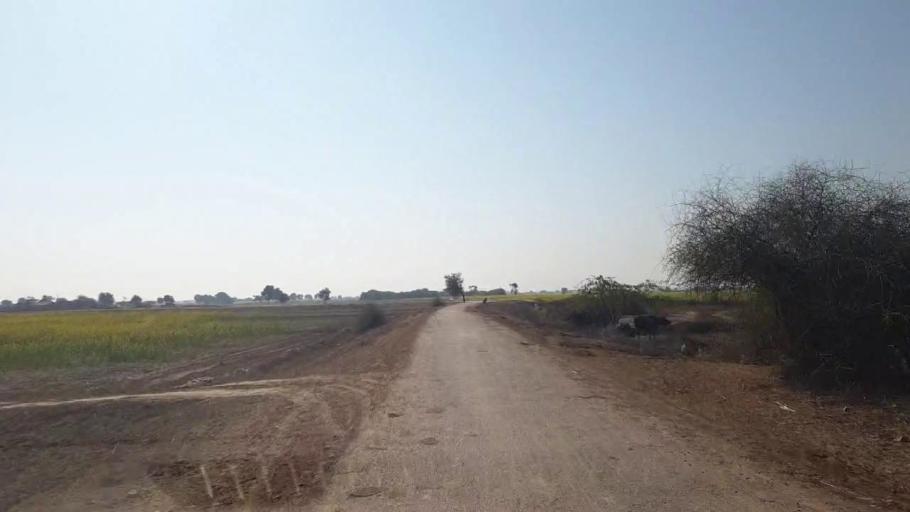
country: PK
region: Sindh
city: Shahpur Chakar
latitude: 26.0837
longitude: 68.6233
